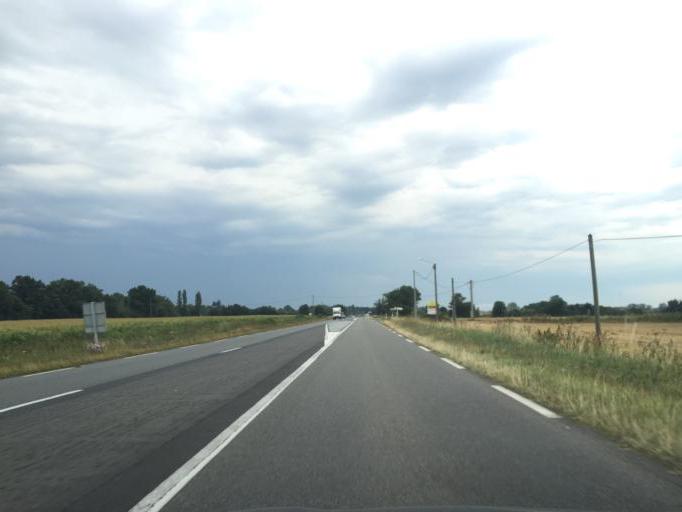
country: FR
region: Auvergne
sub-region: Departement de l'Allier
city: Varennes-sur-Allier
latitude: 46.3620
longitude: 3.3699
